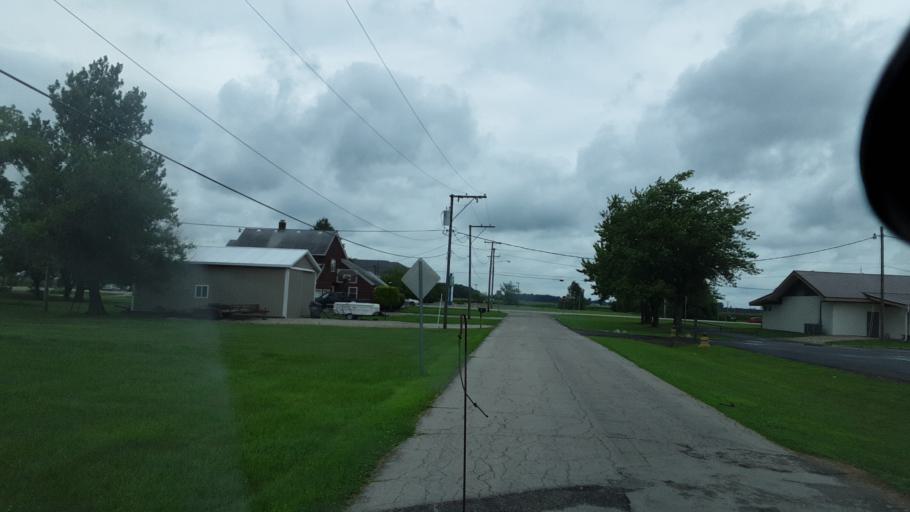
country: US
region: Indiana
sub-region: Jay County
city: Portland
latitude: 40.4379
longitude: -84.9935
